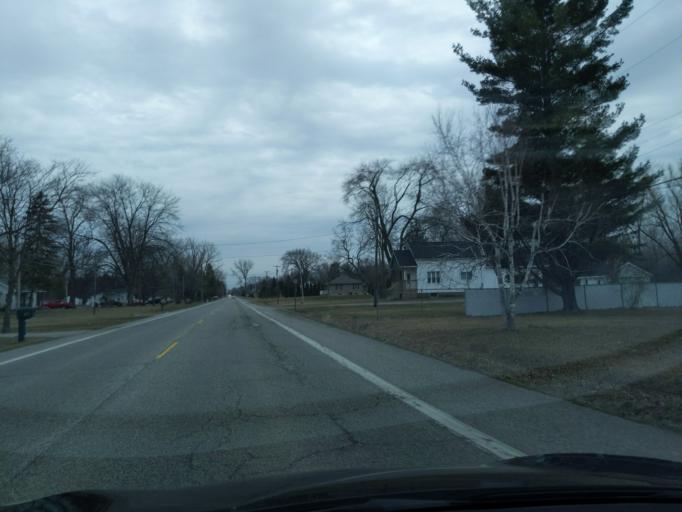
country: US
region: Michigan
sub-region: Bay County
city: Bay City
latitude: 43.6522
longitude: -83.9126
